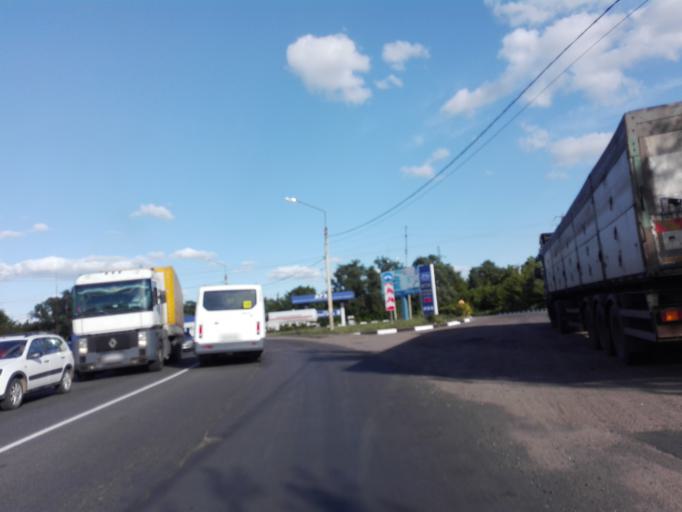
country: RU
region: Orjol
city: Orel
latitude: 52.9360
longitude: 36.0589
